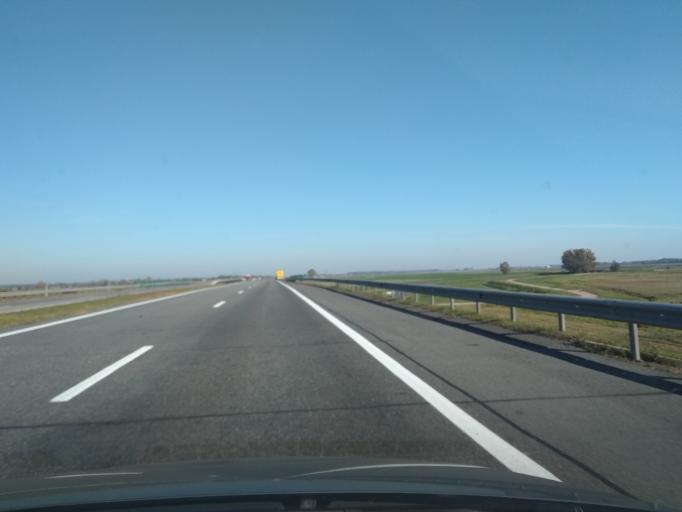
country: BY
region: Brest
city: Byaroza
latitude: 52.4205
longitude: 24.8233
